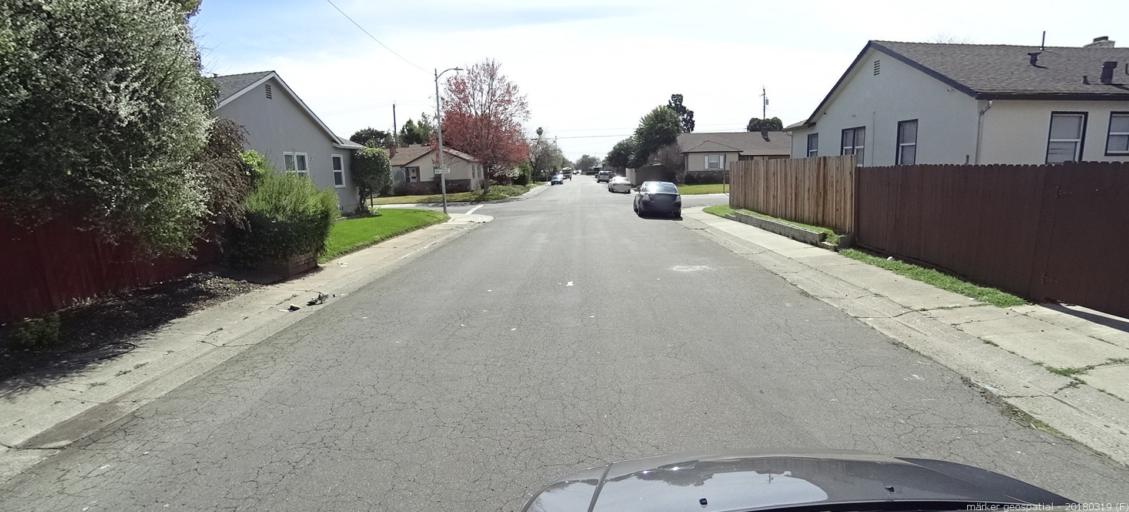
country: US
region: California
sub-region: Sacramento County
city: Parkway
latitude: 38.5170
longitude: -121.4528
